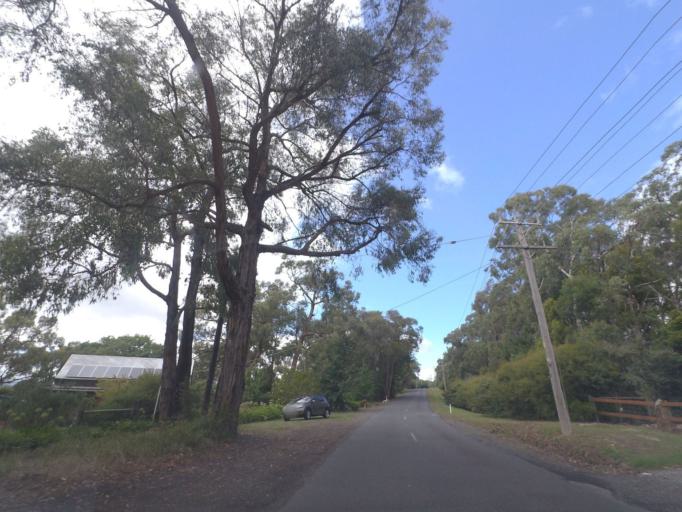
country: AU
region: Victoria
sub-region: Yarra Ranges
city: Woori Yallock
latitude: -37.7775
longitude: 145.5528
